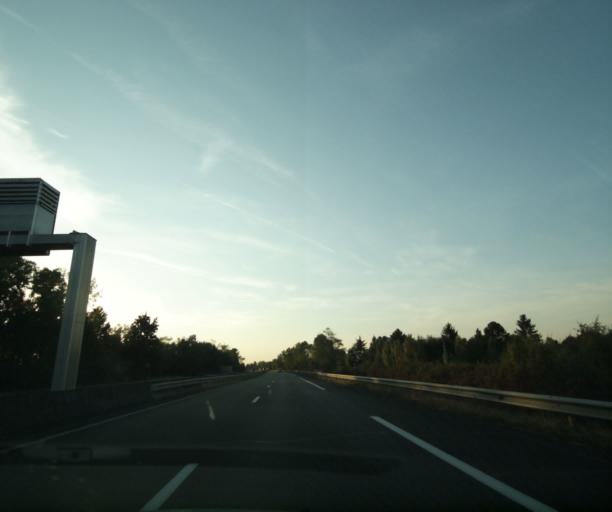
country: FR
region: Aquitaine
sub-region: Departement du Lot-et-Garonne
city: Roquefort
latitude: 44.1812
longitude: 0.5641
